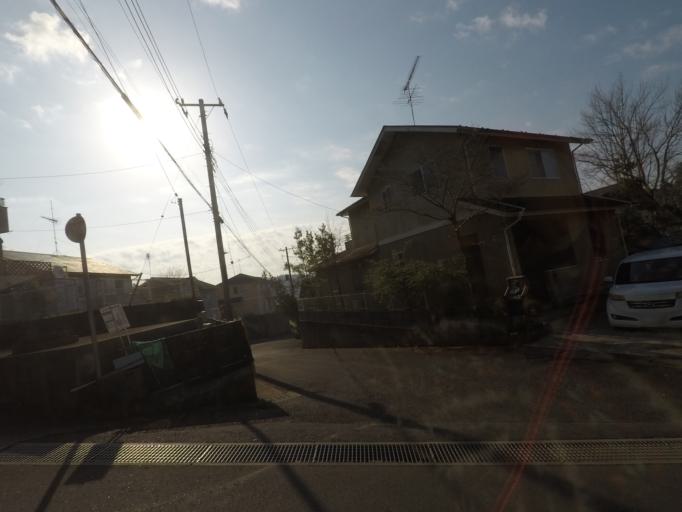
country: JP
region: Chiba
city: Yachimata
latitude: 35.6387
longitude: 140.2864
